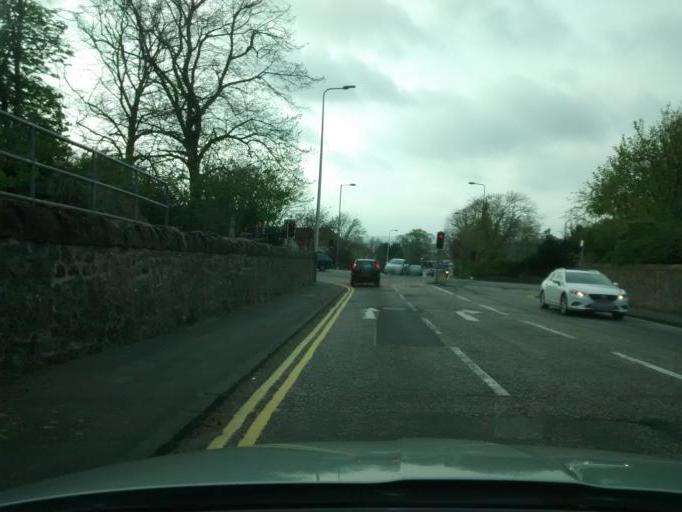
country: GB
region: Scotland
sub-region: Edinburgh
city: Colinton
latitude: 55.9198
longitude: -3.2394
